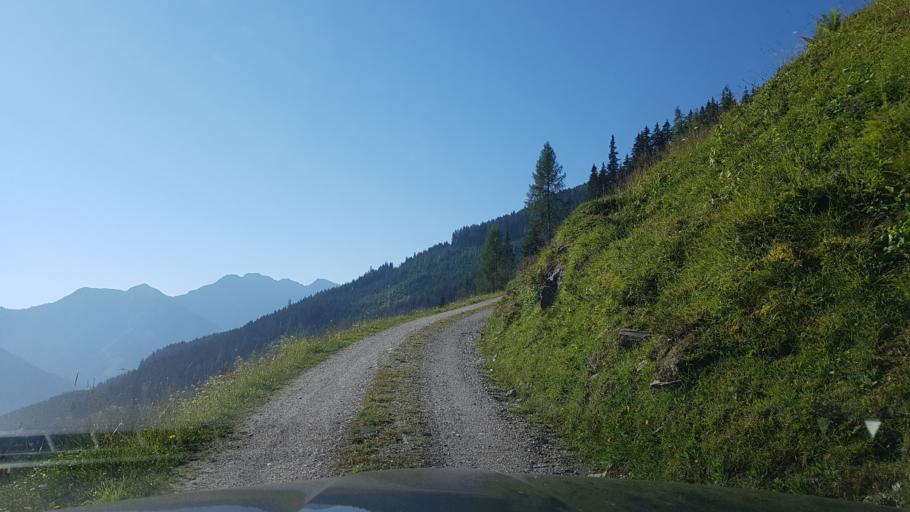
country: AT
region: Salzburg
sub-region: Politischer Bezirk Sankt Johann im Pongau
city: Dorfgastein
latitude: 47.2458
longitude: 13.0731
